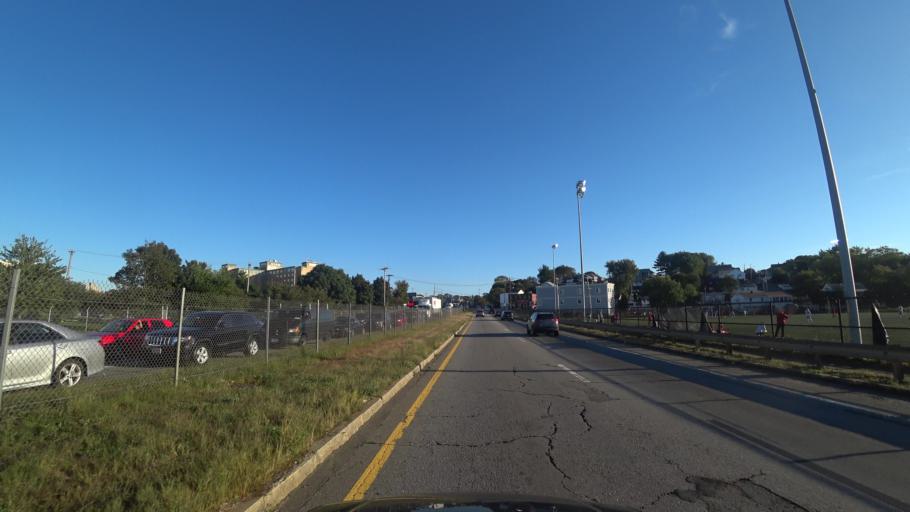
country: US
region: Massachusetts
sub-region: Suffolk County
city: Revere
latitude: 42.4132
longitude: -71.0033
